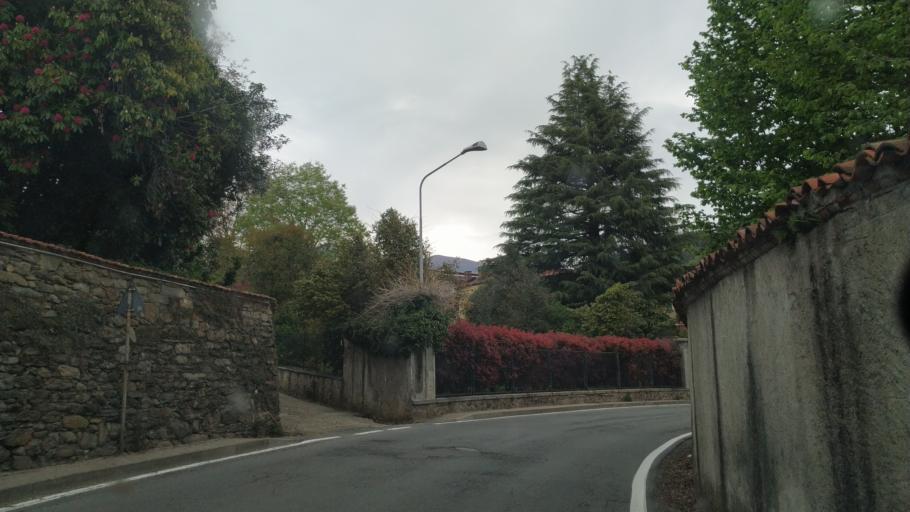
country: IT
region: Piedmont
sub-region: Provincia di Biella
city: Pollone
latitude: 45.5808
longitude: 8.0057
